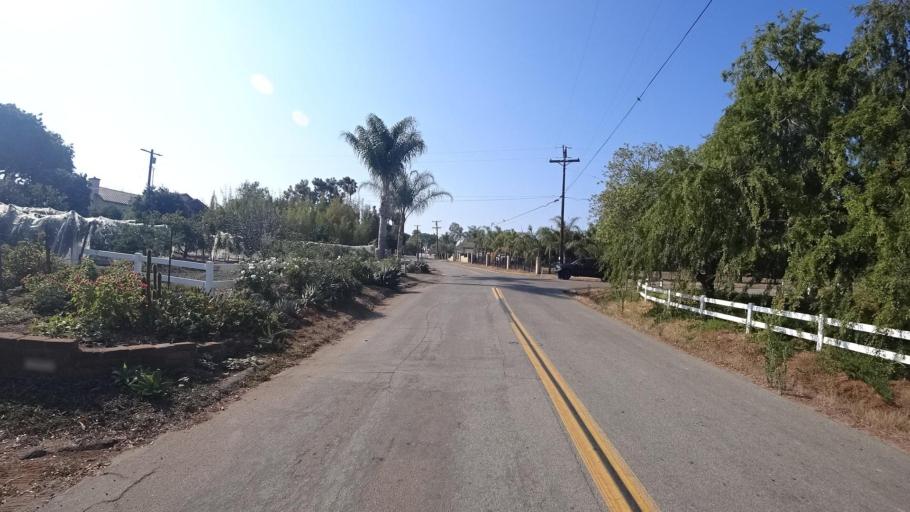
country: US
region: California
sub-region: San Diego County
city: Vista
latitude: 33.2344
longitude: -117.2351
